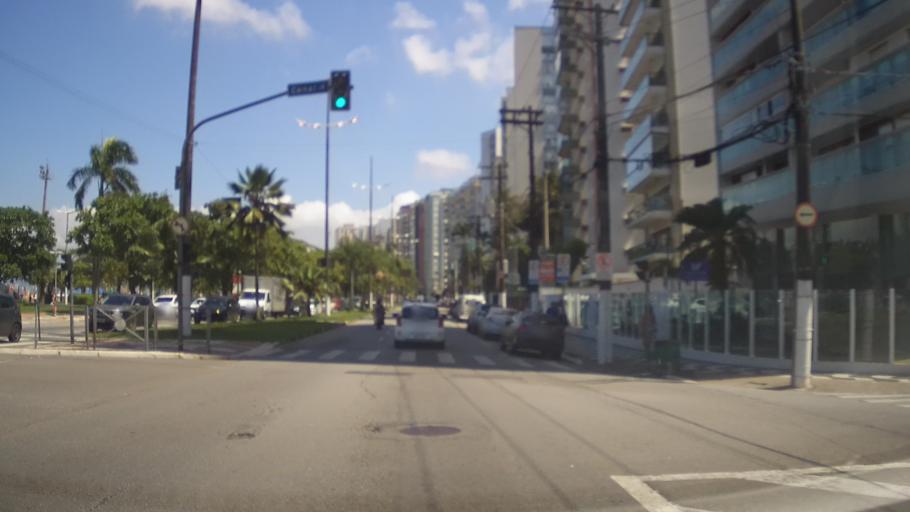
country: BR
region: Sao Paulo
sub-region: Santos
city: Santos
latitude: -23.9741
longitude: -46.3212
